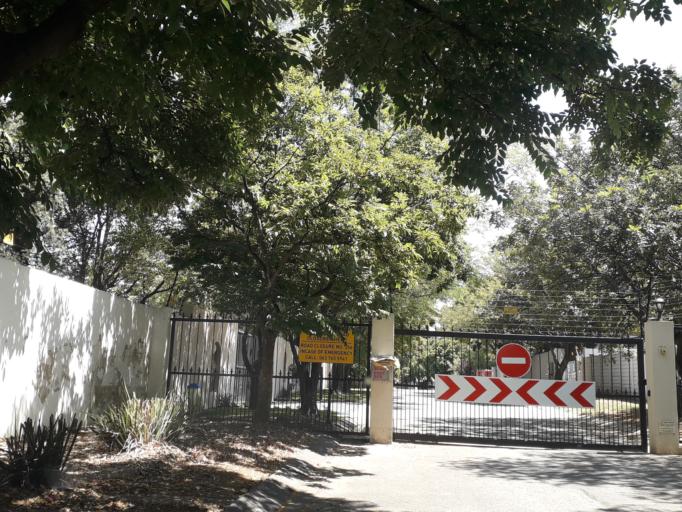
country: ZA
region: Gauteng
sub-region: City of Johannesburg Metropolitan Municipality
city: Diepsloot
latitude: -26.0451
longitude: 27.9901
